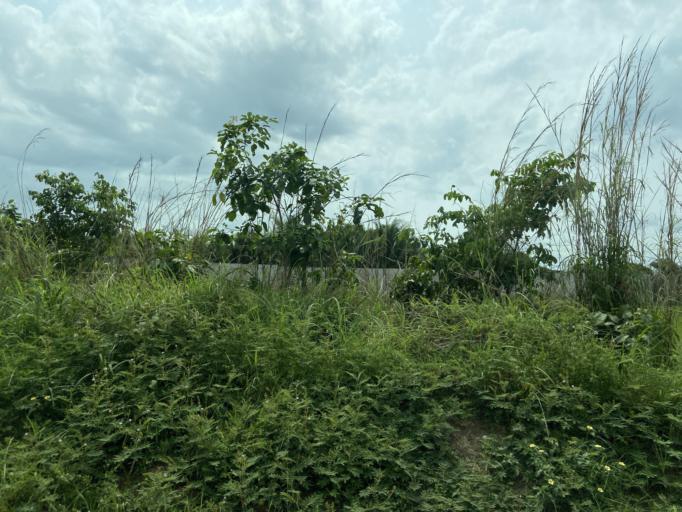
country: BR
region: Para
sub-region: Maraba
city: Maraba
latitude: -5.2970
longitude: -49.0667
